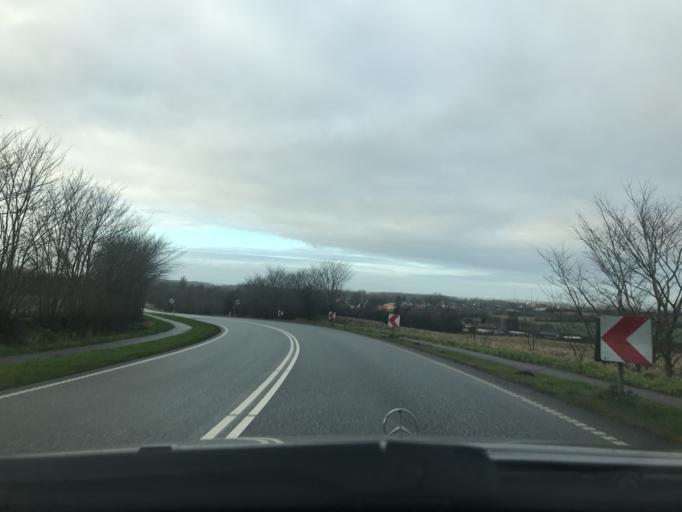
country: DK
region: South Denmark
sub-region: Sonderborg Kommune
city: Dybbol
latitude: 54.9079
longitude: 9.7453
